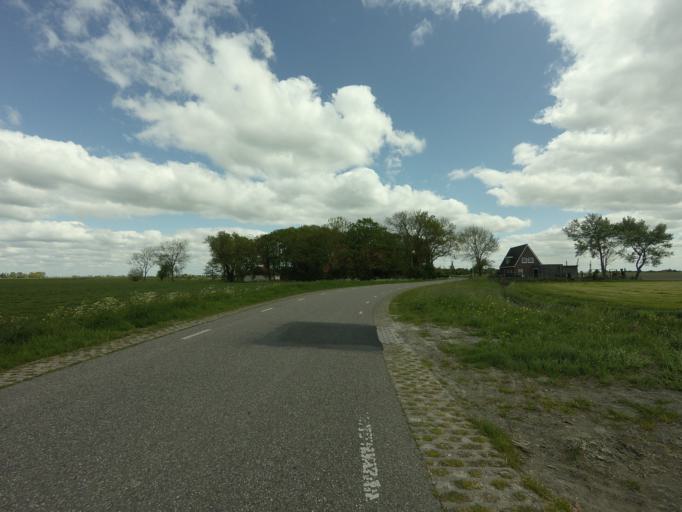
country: NL
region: Friesland
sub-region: Sudwest Fryslan
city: Bolsward
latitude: 53.0914
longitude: 5.5399
